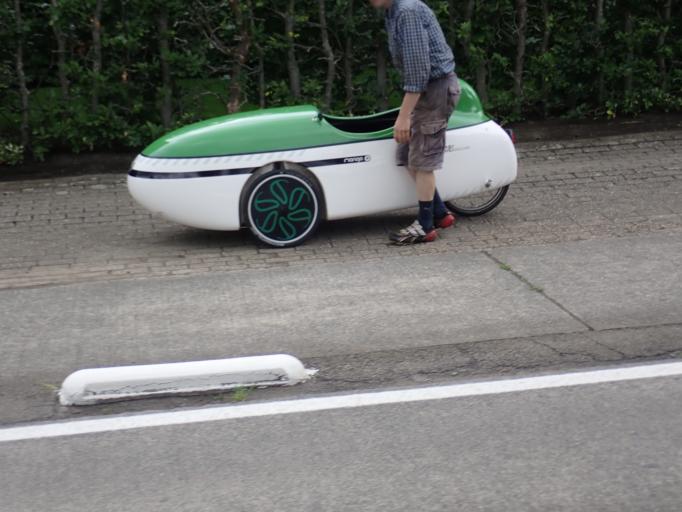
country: BE
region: Flanders
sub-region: Provincie Antwerpen
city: Berlaar
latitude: 51.1164
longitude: 4.6989
